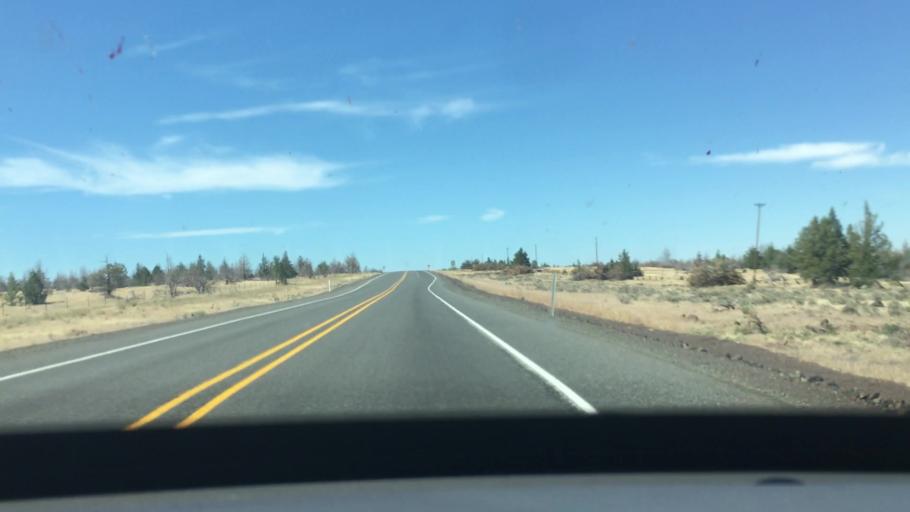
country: US
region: Oregon
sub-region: Jefferson County
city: Madras
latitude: 44.8990
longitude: -120.9370
